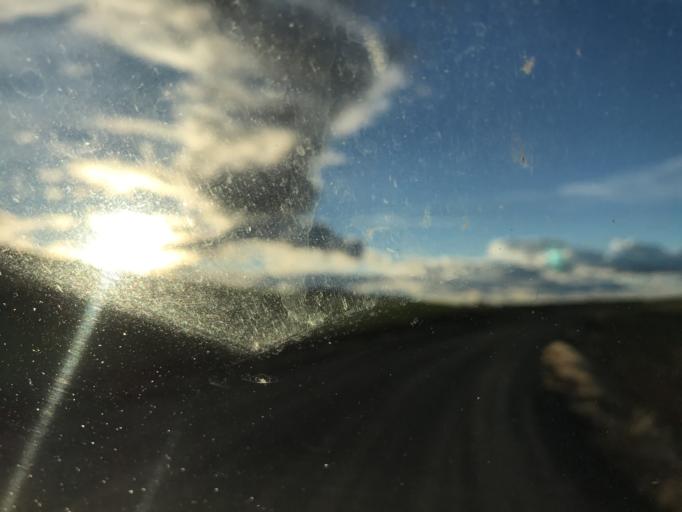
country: US
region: Idaho
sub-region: Latah County
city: Moscow
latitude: 46.7663
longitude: -116.9890
